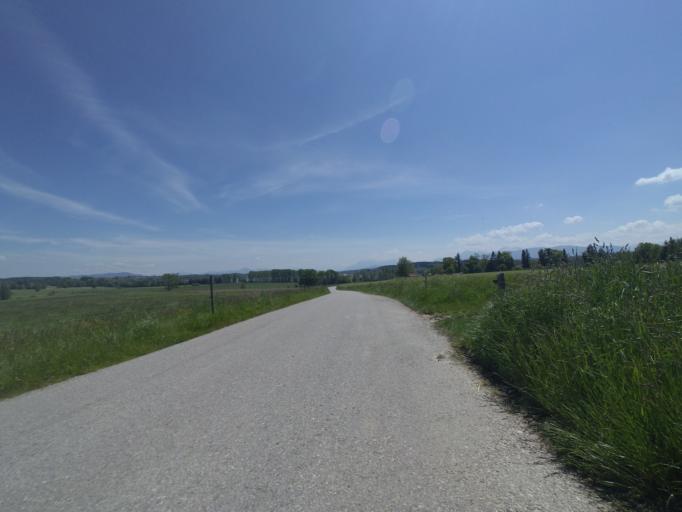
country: DE
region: Bavaria
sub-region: Upper Bavaria
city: Waging am See
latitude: 47.9510
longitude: 12.7559
